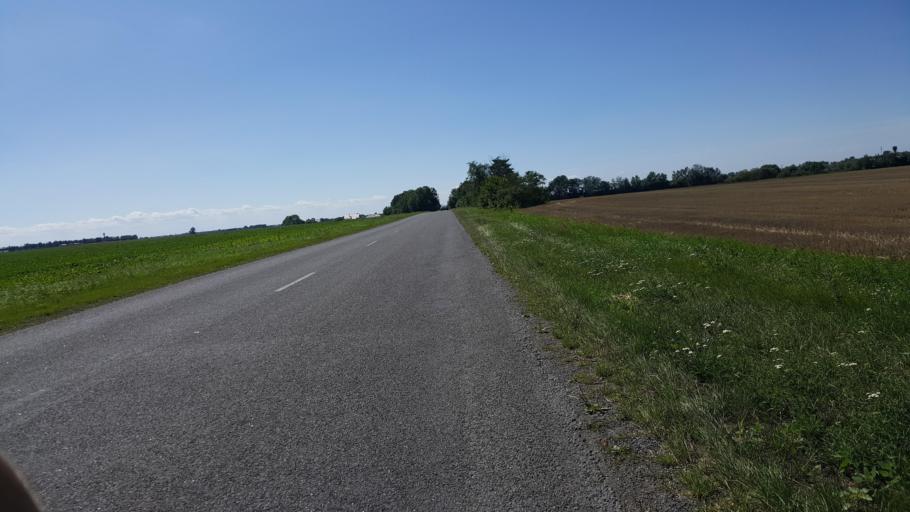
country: BY
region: Brest
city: Charnawchytsy
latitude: 52.2053
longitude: 23.7740
